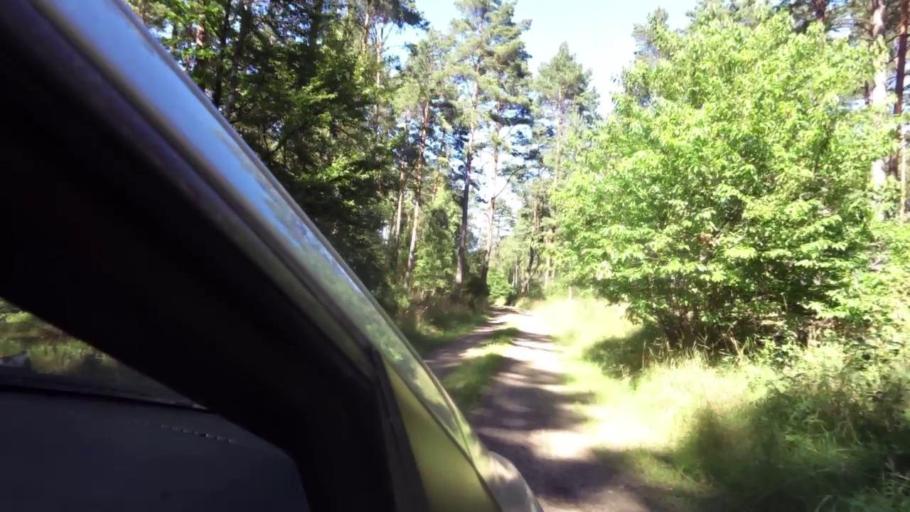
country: PL
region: West Pomeranian Voivodeship
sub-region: Powiat szczecinecki
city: Bialy Bor
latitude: 53.8225
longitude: 16.8657
